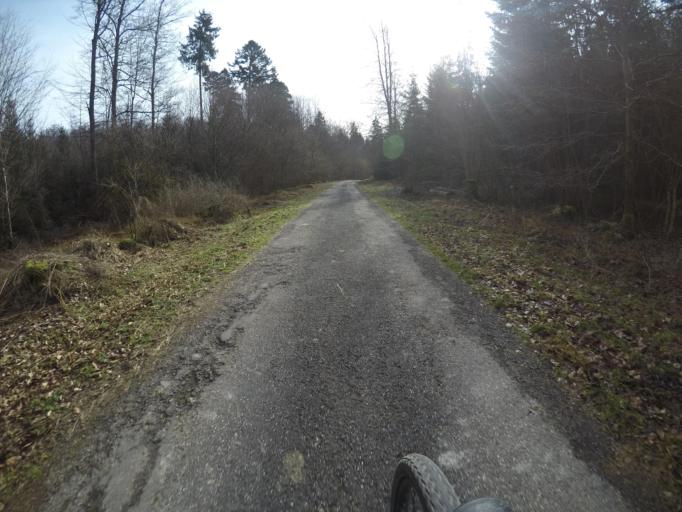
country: DE
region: Baden-Wuerttemberg
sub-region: Karlsruhe Region
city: Calw
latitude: 48.6725
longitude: 8.7737
